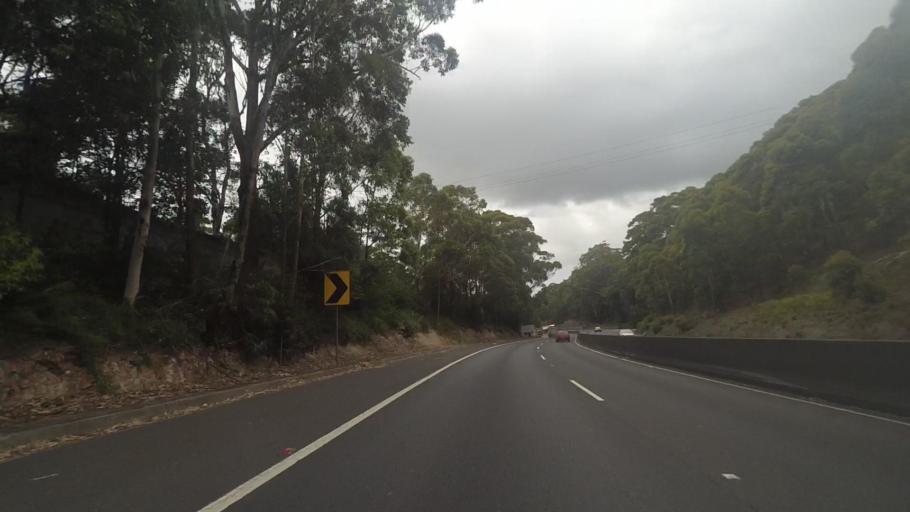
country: AU
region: New South Wales
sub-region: Wollongong
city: Mount Ousley
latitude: -34.3981
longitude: 150.8685
